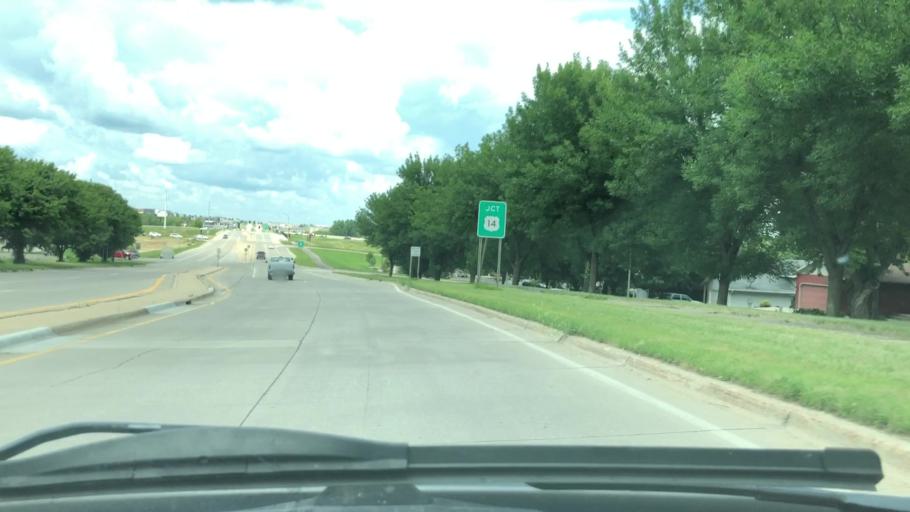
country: US
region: Minnesota
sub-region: Olmsted County
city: Rochester
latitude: 44.0330
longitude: -92.5164
